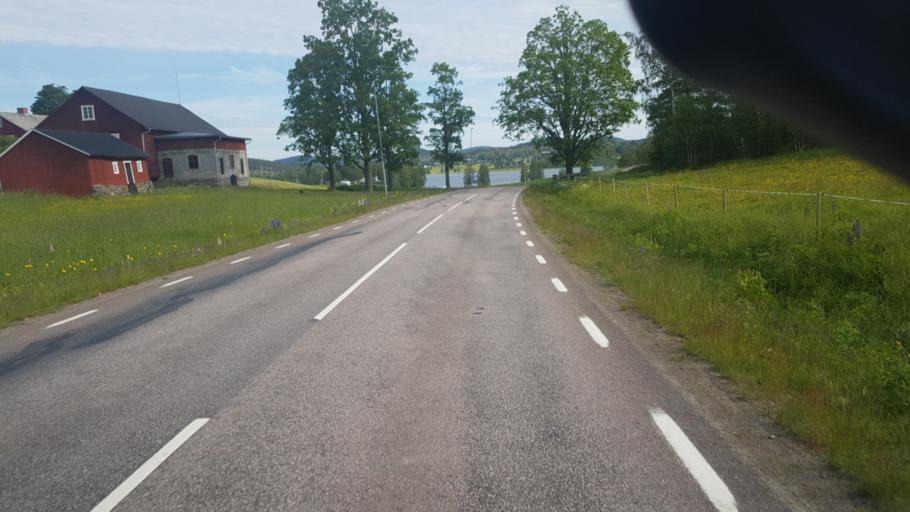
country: SE
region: Vaermland
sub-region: Arvika Kommun
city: Arvika
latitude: 59.7764
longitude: 12.6160
